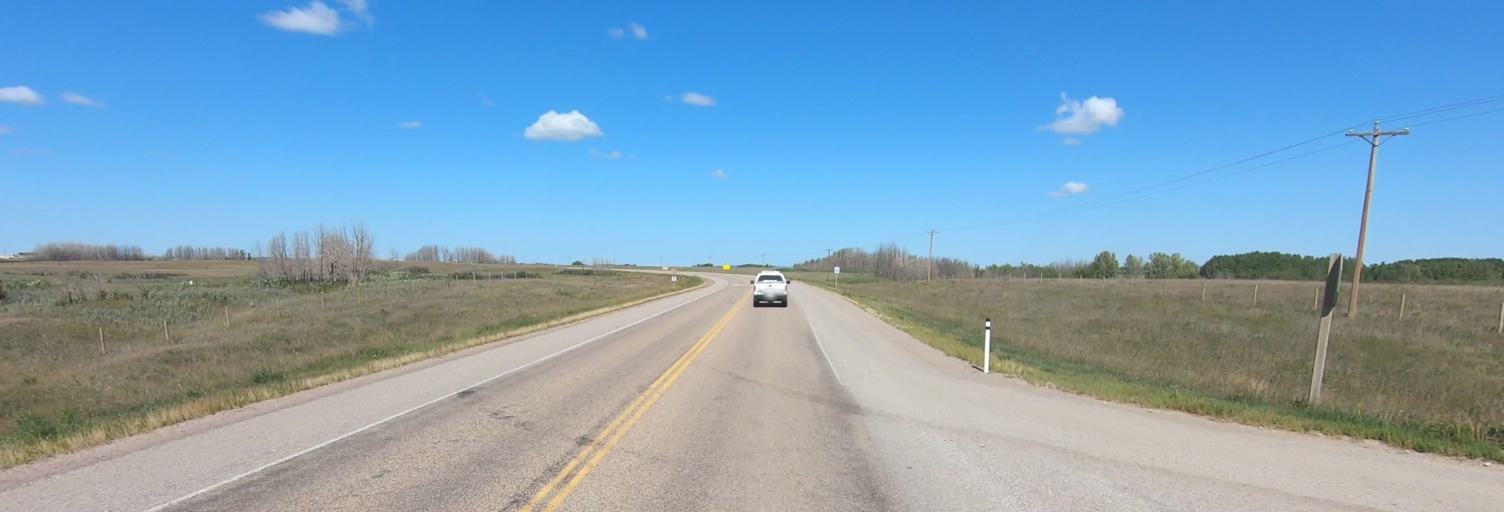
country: CA
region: Alberta
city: Strathmore
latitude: 50.8779
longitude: -113.1676
